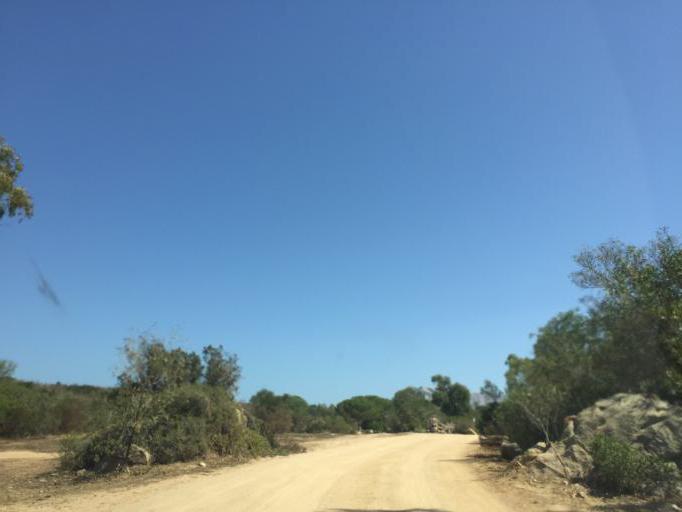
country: IT
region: Sardinia
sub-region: Provincia di Olbia-Tempio
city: San Teodoro
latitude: 40.8340
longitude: 9.6802
